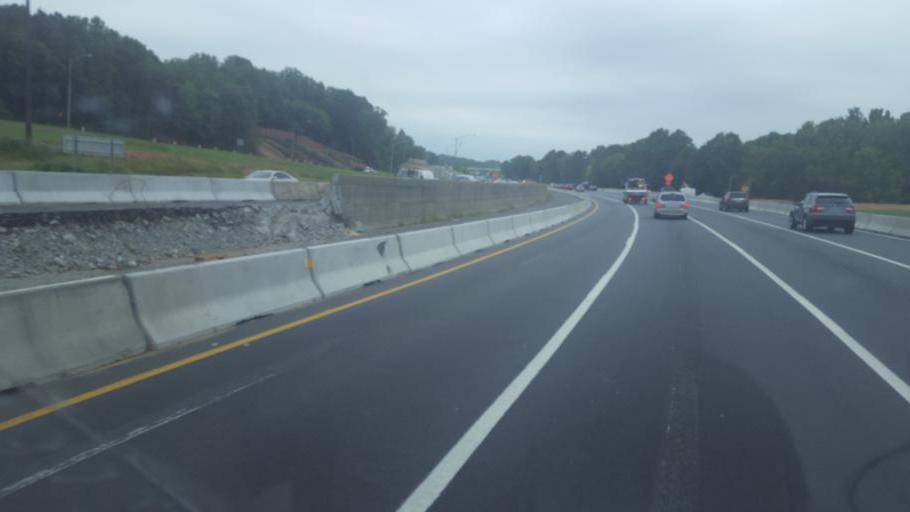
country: US
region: North Carolina
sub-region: Mecklenburg County
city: Charlotte
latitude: 35.2612
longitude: -80.8407
